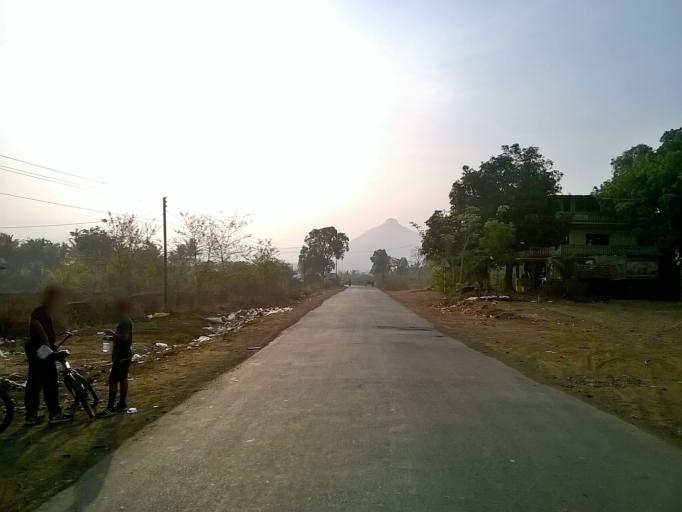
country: IN
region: Maharashtra
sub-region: Raigarh
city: Kalundri
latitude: 19.0180
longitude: 73.1914
